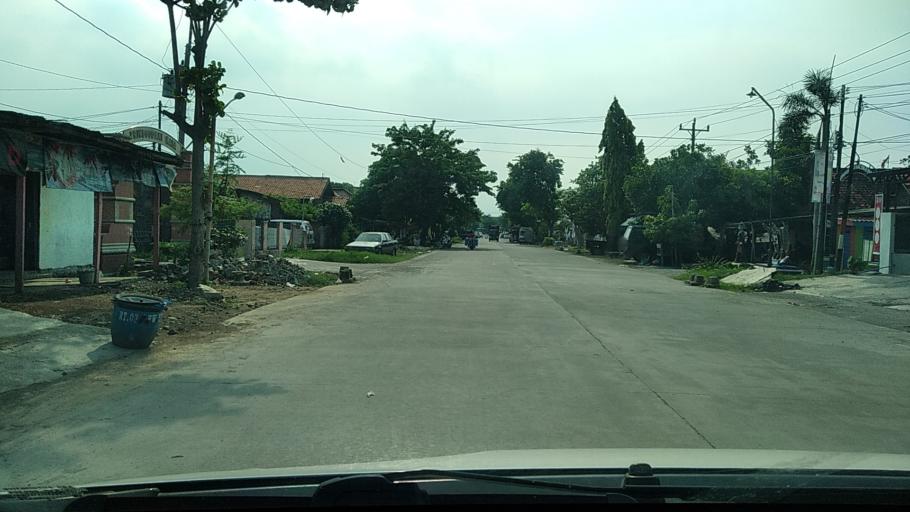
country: ID
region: Central Java
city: Semarang
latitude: -6.9737
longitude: 110.3960
